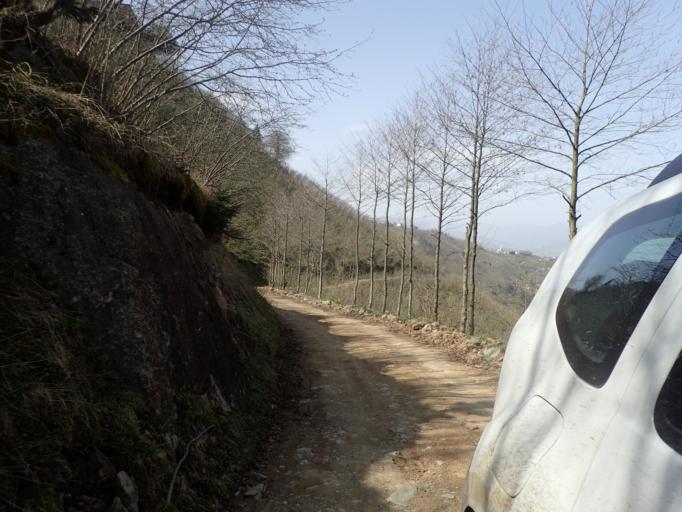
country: TR
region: Ordu
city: Kabaduz
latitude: 40.8233
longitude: 37.8746
